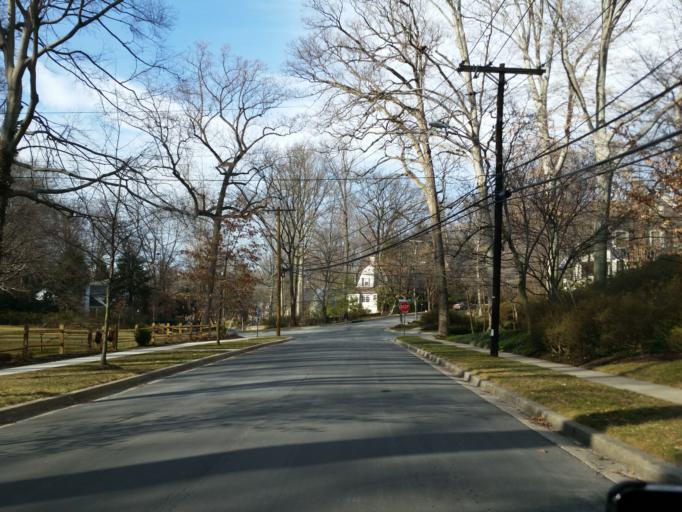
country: US
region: Maryland
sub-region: Montgomery County
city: Chevy Chase
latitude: 38.9824
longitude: -77.0814
